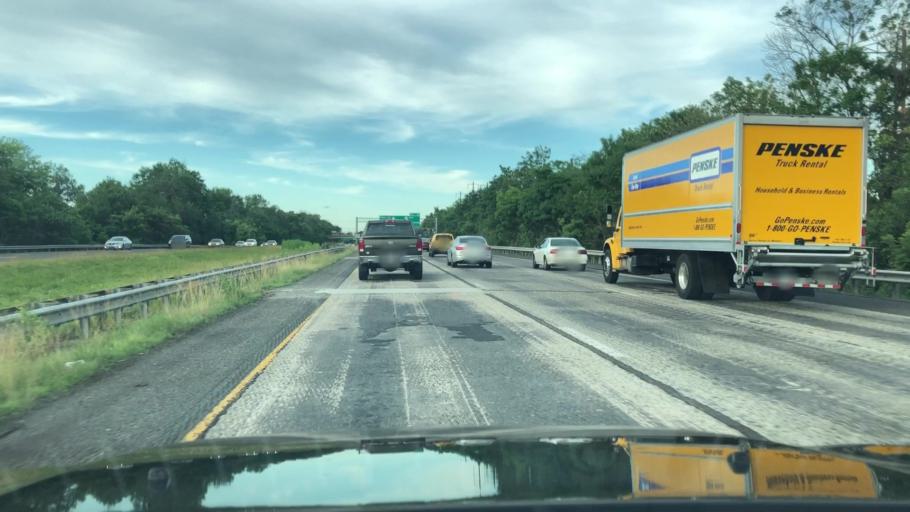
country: US
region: New Jersey
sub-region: Burlington County
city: Delanco
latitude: 40.0616
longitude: -74.9753
